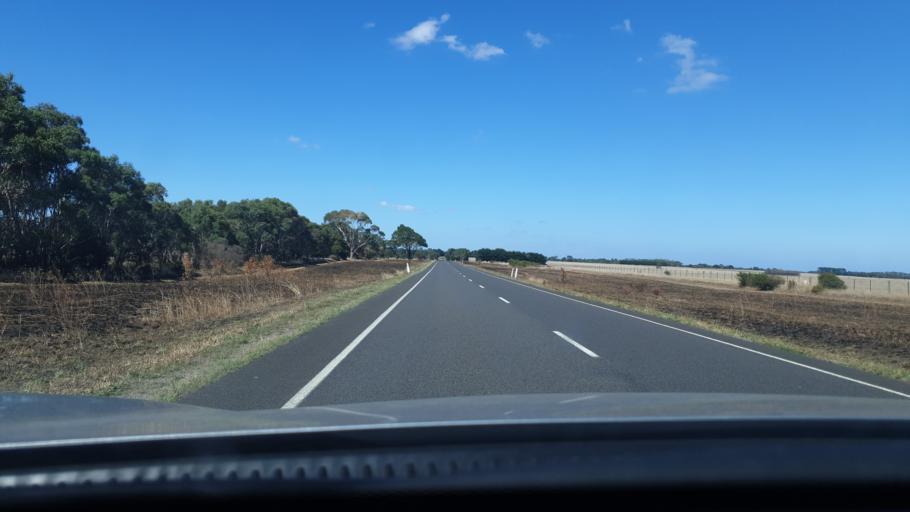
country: AU
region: Victoria
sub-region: Warrnambool
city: Warrnambool
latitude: -38.1727
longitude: 142.4082
